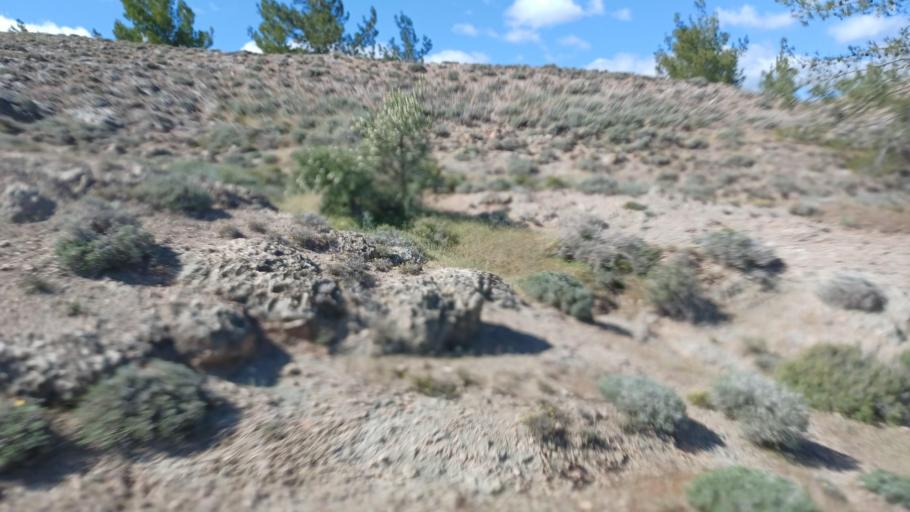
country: CY
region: Lefkosia
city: Peristerona
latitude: 35.0593
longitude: 33.0573
